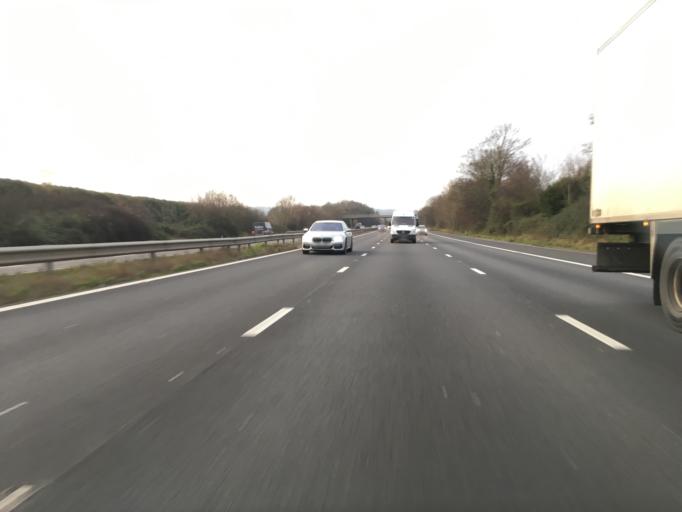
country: GB
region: England
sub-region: Gloucestershire
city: Barnwood
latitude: 51.8481
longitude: -2.1845
